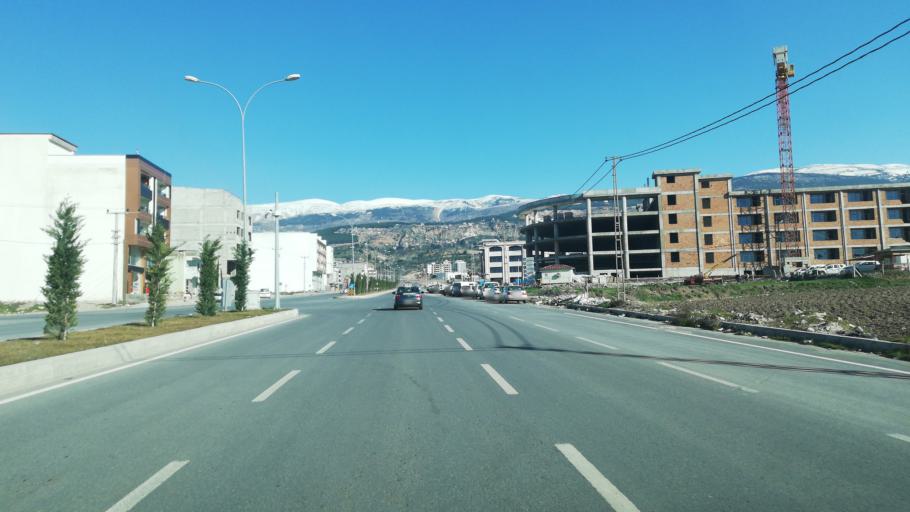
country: TR
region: Kahramanmaras
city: Kahramanmaras
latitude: 37.5744
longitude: 36.9746
